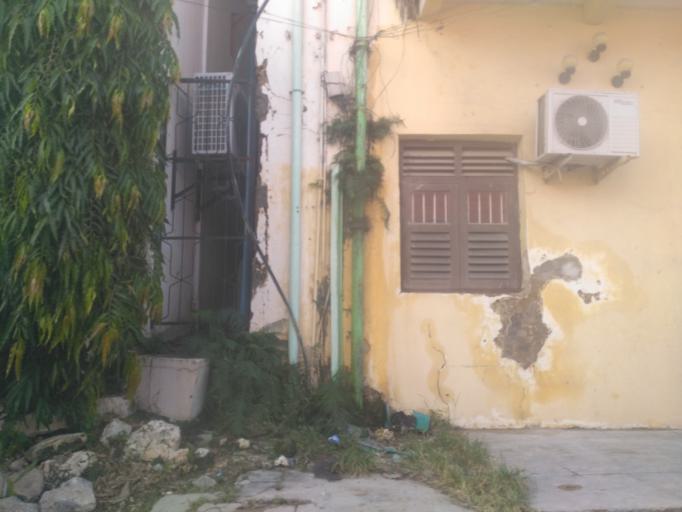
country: TZ
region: Zanzibar Urban/West
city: Zanzibar
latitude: -6.1579
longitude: 39.1930
